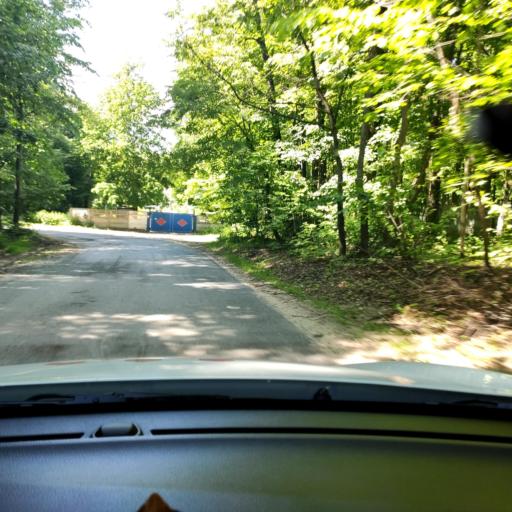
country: RU
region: Tatarstan
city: Osinovo
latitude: 55.7806
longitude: 48.7982
